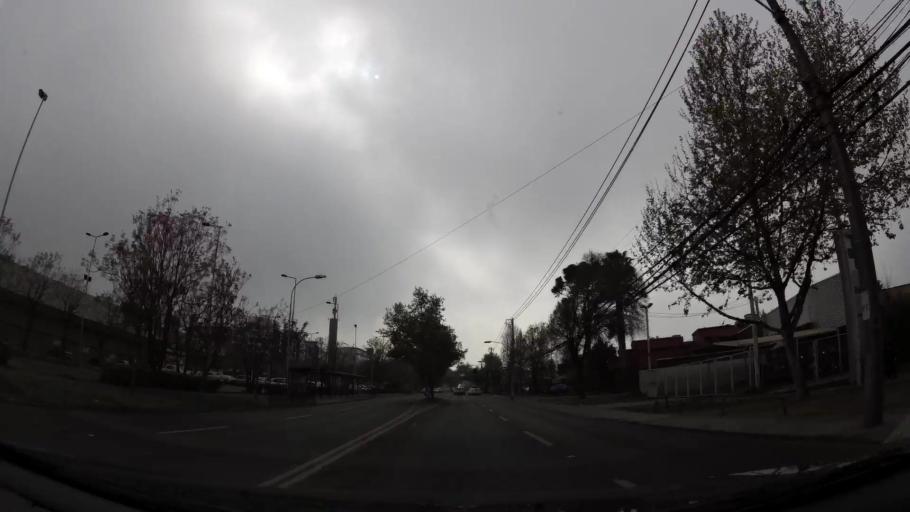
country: CL
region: Santiago Metropolitan
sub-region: Provincia de Santiago
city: Villa Presidente Frei, Nunoa, Santiago, Chile
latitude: -33.3850
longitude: -70.5543
